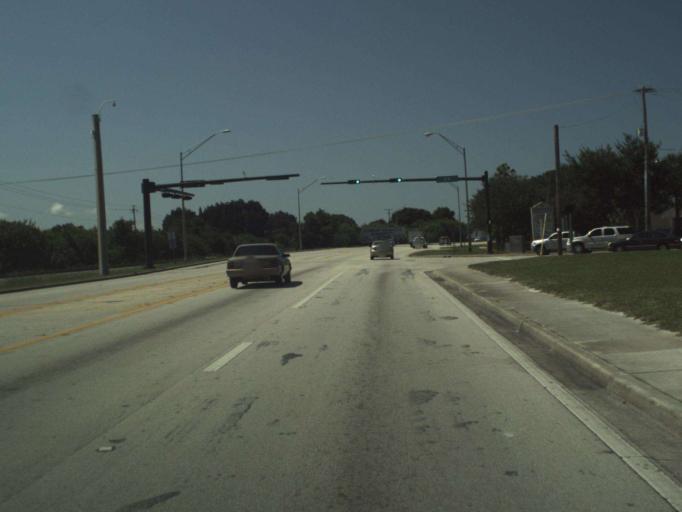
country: US
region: Florida
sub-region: Indian River County
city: Gifford
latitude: 27.6597
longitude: -80.4038
